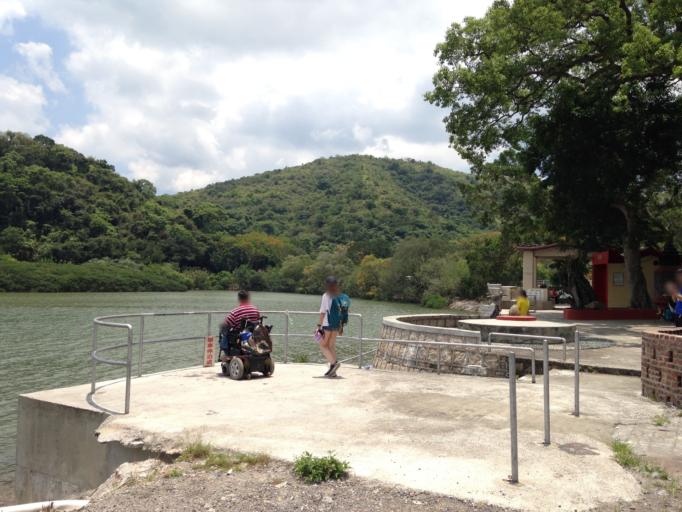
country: CN
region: Guangdong
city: Haishan
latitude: 22.5248
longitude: 114.2085
